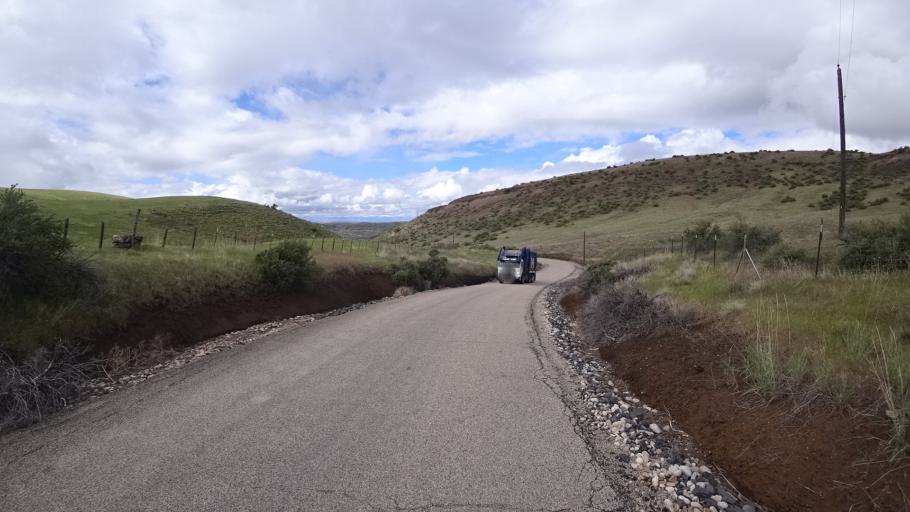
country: US
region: Idaho
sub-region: Ada County
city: Garden City
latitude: 43.7358
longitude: -116.2275
